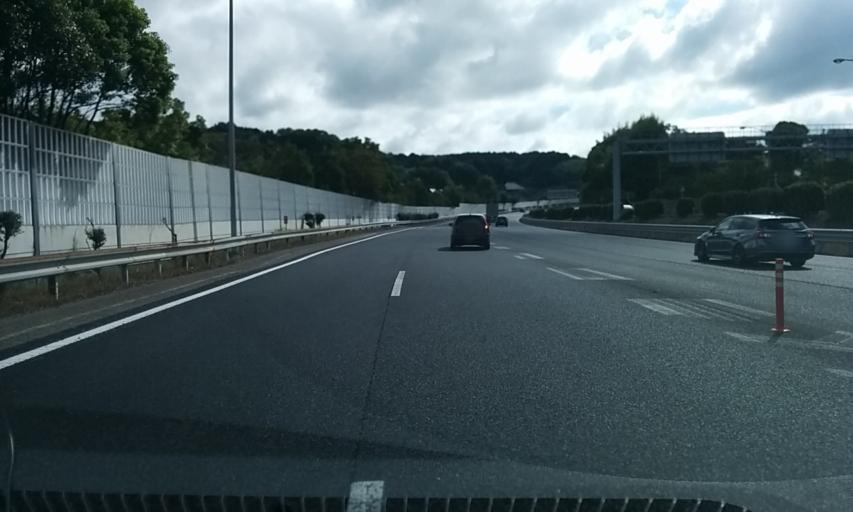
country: JP
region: Hyogo
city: Sandacho
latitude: 34.8933
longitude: 135.1542
